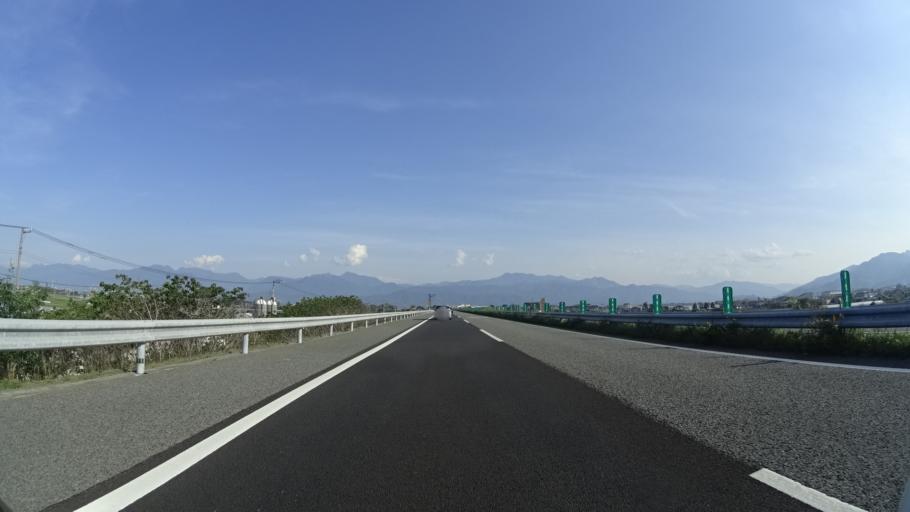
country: JP
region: Ehime
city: Saijo
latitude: 33.9572
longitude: 133.0664
